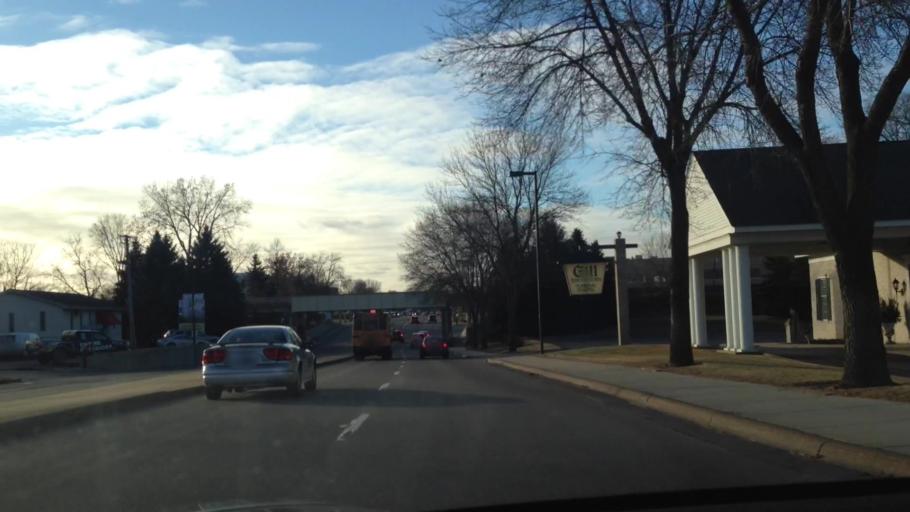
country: US
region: Minnesota
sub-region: Hennepin County
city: Crystal
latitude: 45.0330
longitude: -93.3735
